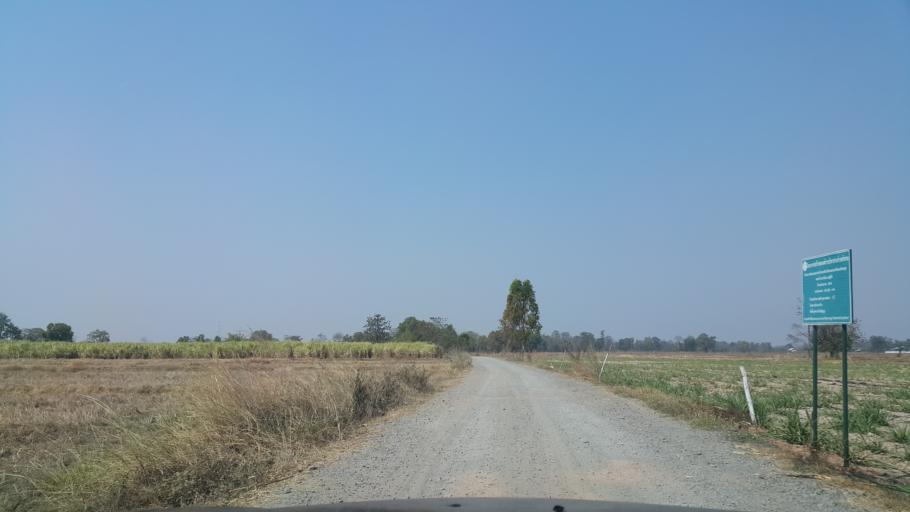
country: TH
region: Buriram
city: Krasang
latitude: 15.0907
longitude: 103.3806
